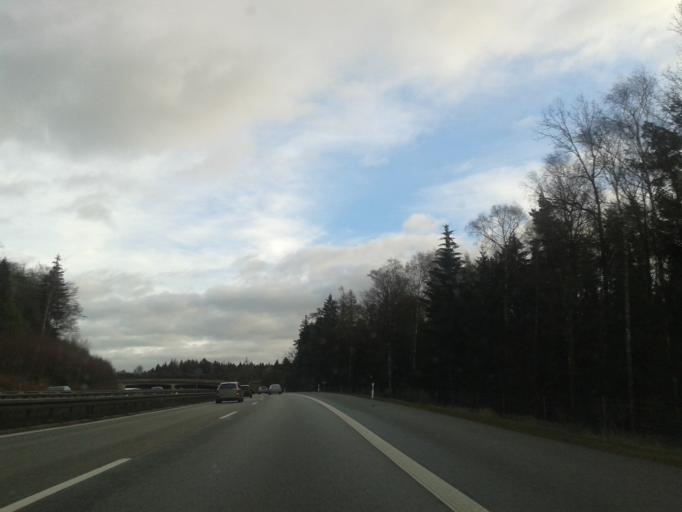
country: DE
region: Saxony
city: Rammenau
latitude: 51.1732
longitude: 14.1220
